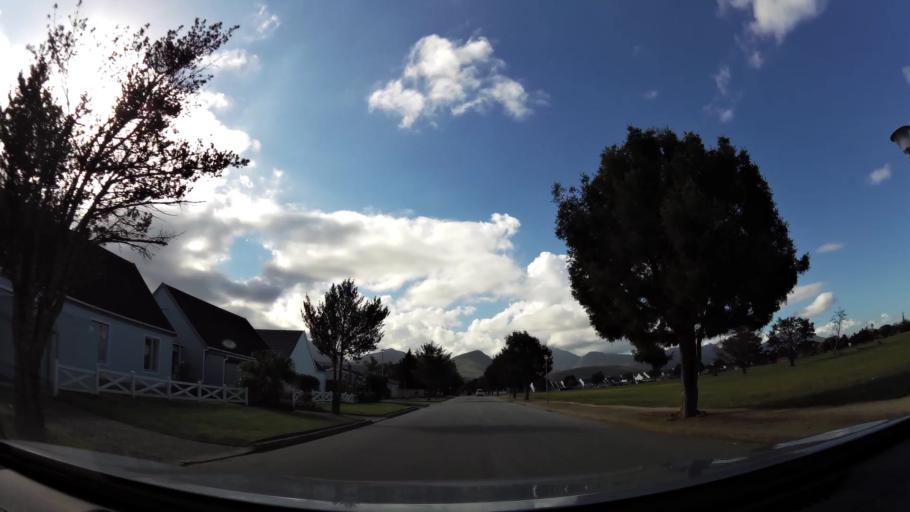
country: ZA
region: Western Cape
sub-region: Eden District Municipality
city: George
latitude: -33.9621
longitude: 22.4883
